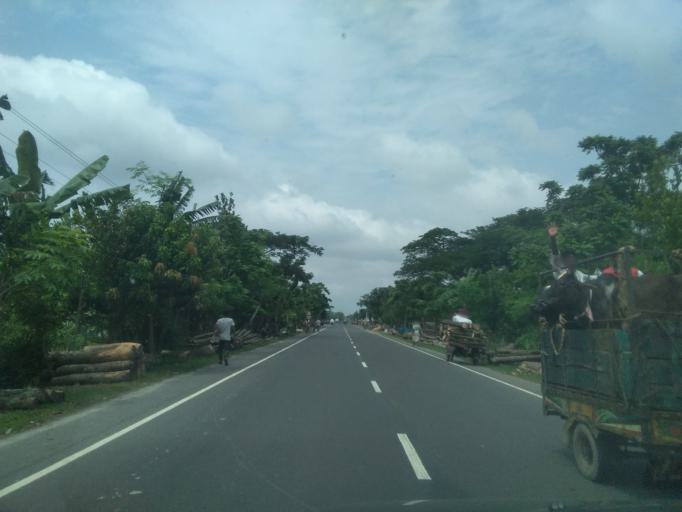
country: BD
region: Khulna
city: Kesabpur
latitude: 22.7938
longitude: 89.2237
